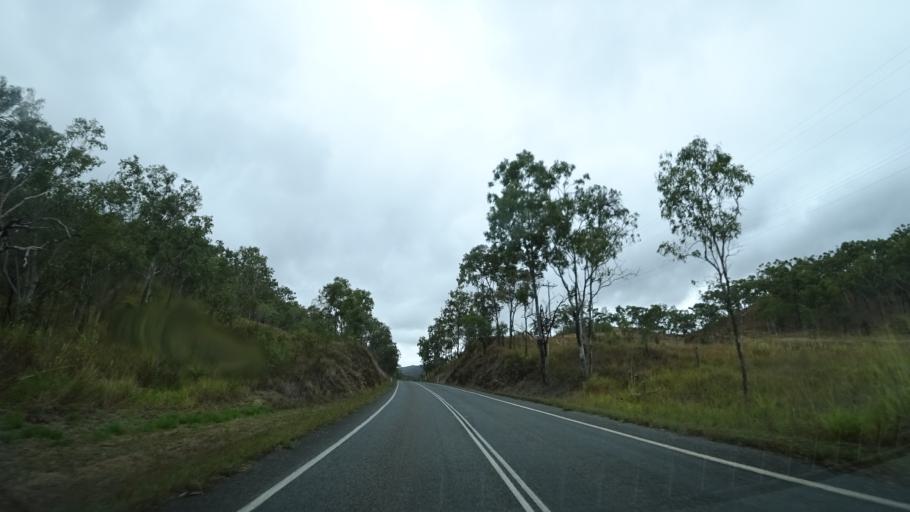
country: AU
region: Queensland
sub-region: Cairns
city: Port Douglas
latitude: -16.7060
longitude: 145.3483
